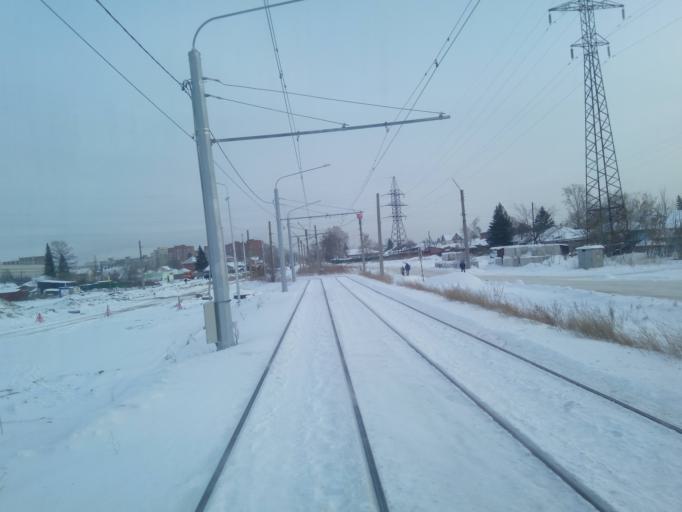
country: RU
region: Novosibirsk
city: Tolmachevo
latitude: 54.9793
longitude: 82.8165
